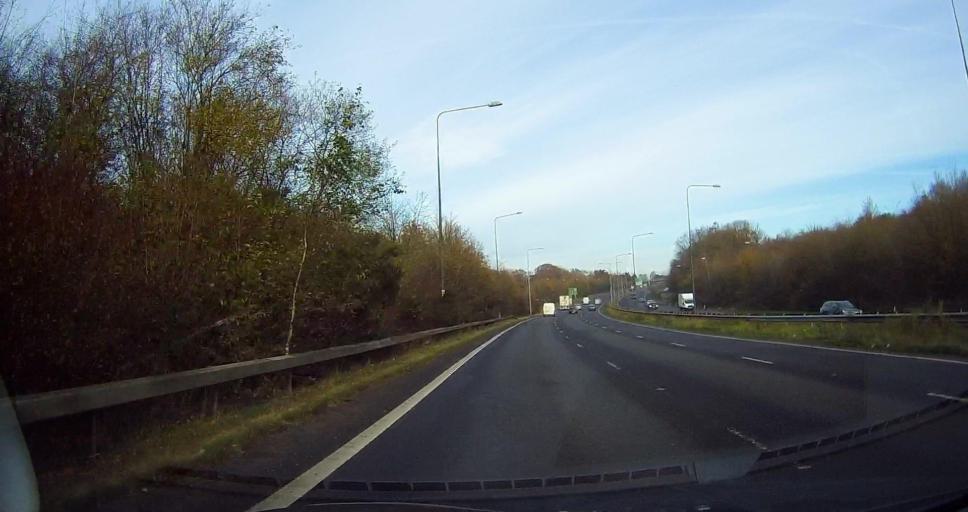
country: GB
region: England
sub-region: West Sussex
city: Cuckfield
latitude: 51.0116
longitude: -0.1979
